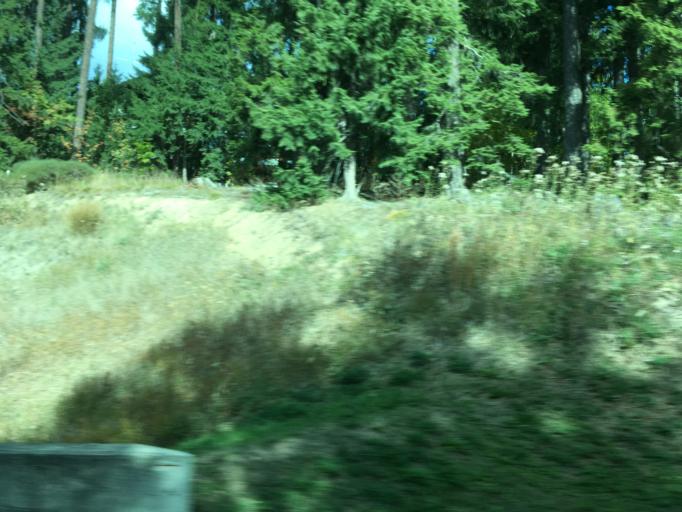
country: CH
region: Valais
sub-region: Sierre District
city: Chermignon-d'en Haut
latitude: 46.2986
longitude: 7.4700
